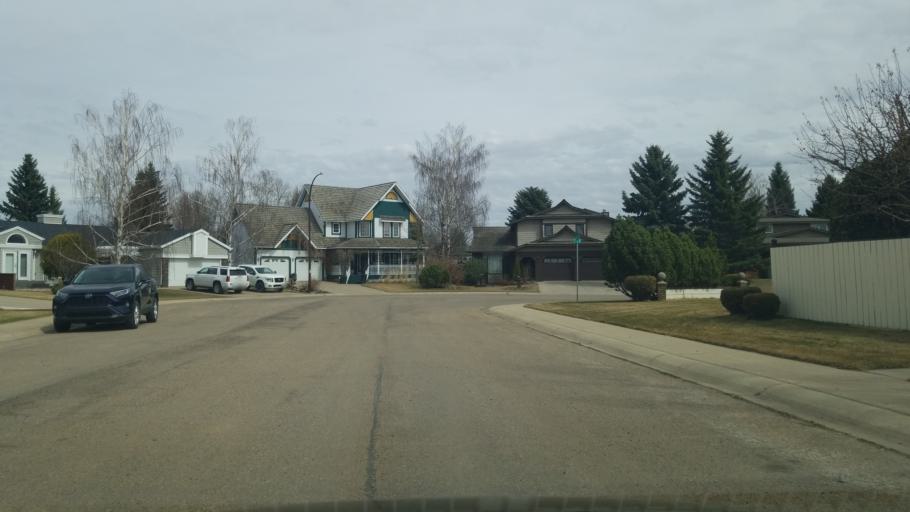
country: CA
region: Saskatchewan
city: Lloydminster
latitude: 53.2729
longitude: -110.0266
